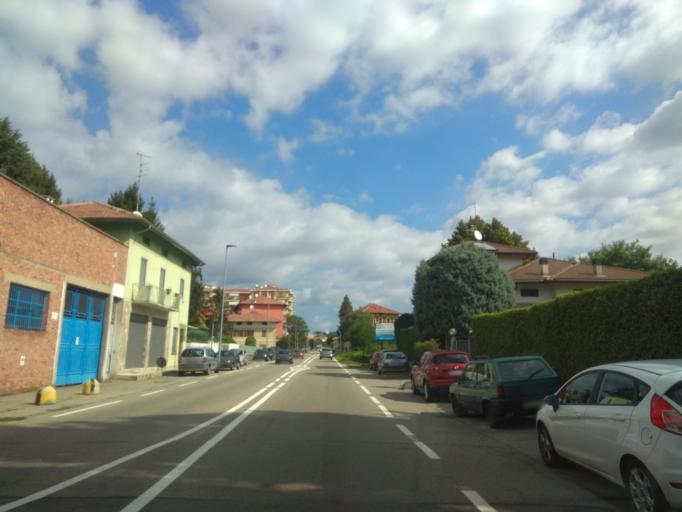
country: IT
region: Piedmont
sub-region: Provincia di Biella
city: Cossato
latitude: 45.5708
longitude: 8.1767
